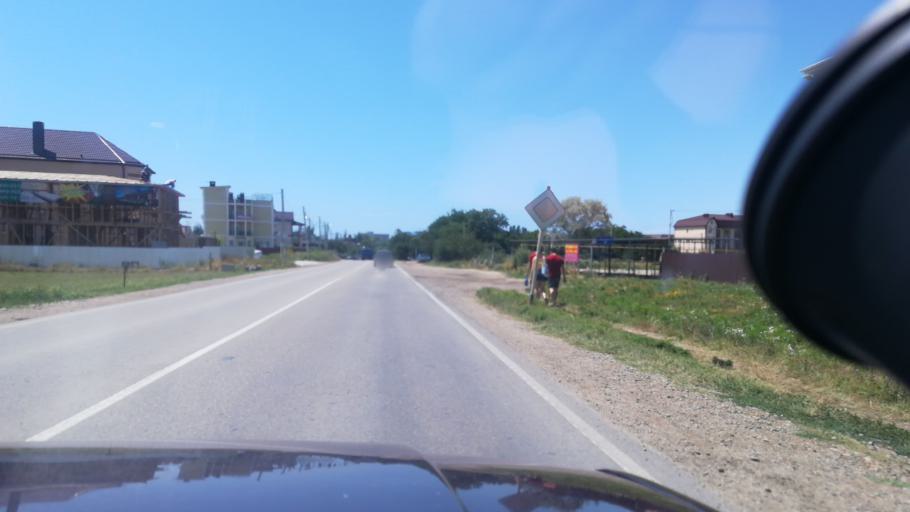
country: RU
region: Krasnodarskiy
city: Vityazevo
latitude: 44.9607
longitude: 37.2999
